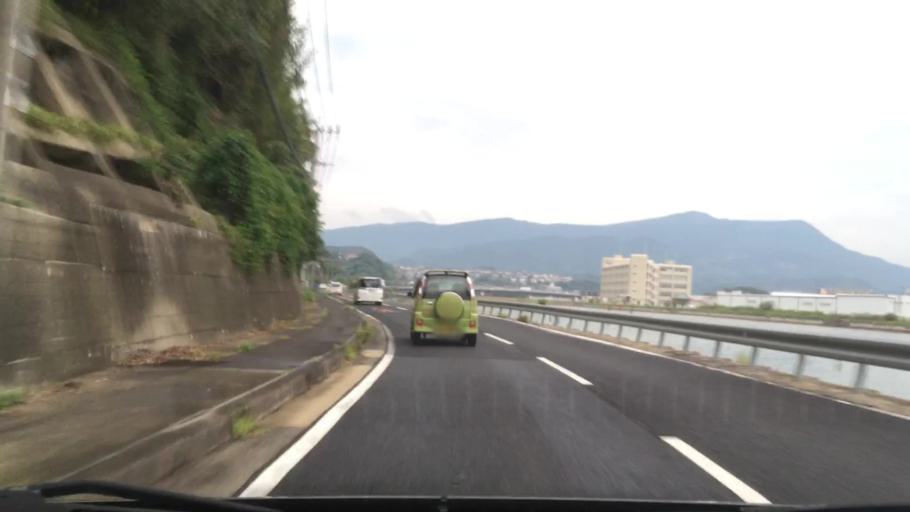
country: JP
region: Nagasaki
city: Sasebo
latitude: 33.1193
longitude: 129.7945
